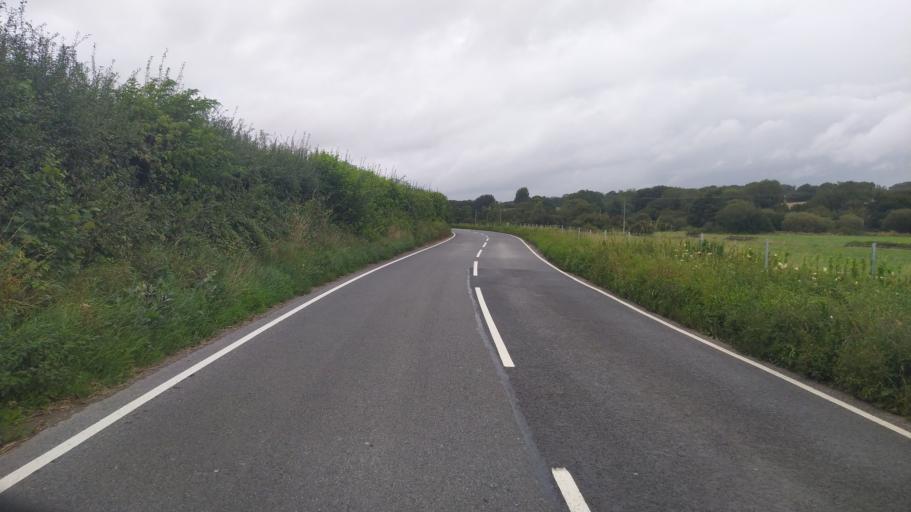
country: GB
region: England
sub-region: Dorset
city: Dorchester
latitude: 50.7549
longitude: -2.3674
